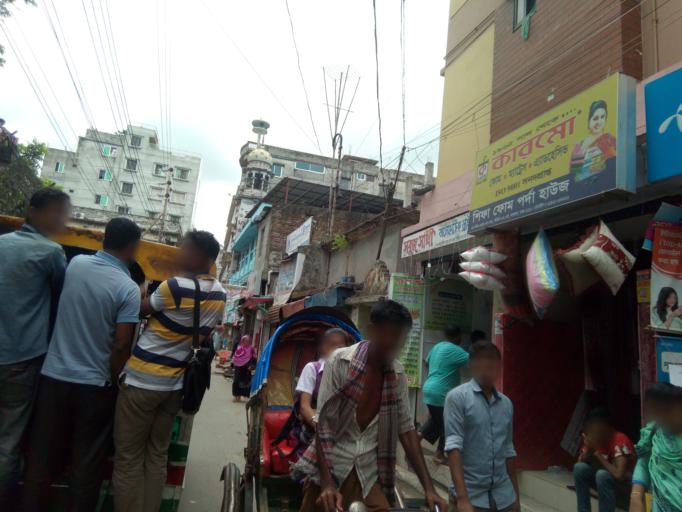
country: BD
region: Dhaka
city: Azimpur
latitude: 23.7256
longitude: 90.3774
